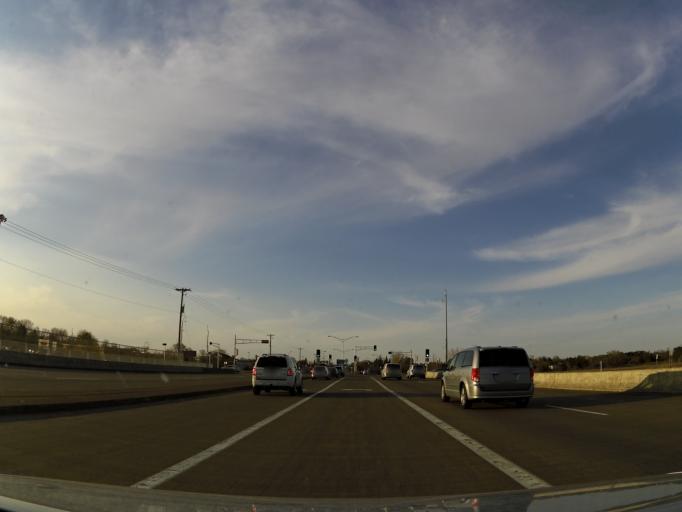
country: US
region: Wisconsin
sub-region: Saint Croix County
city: Hudson
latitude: 44.9632
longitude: -92.7212
